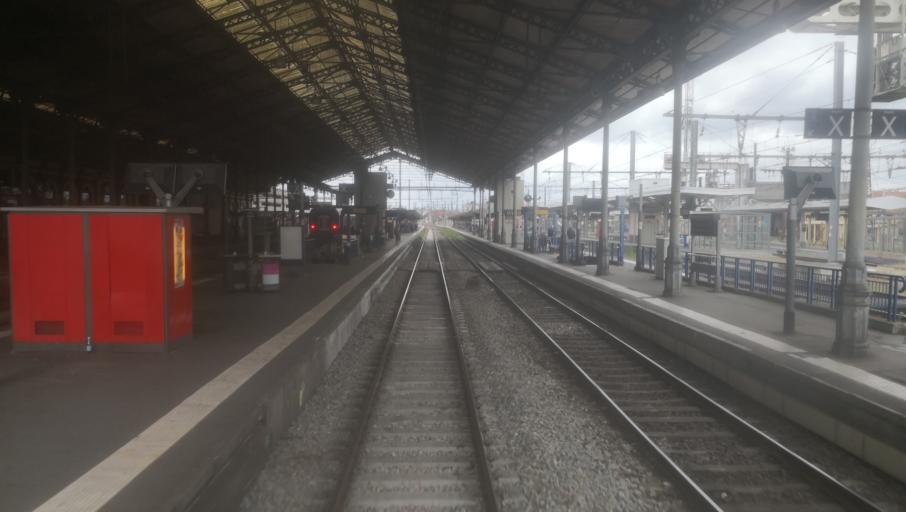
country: FR
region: Midi-Pyrenees
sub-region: Departement de la Haute-Garonne
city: Toulouse
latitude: 43.6124
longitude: 1.4541
